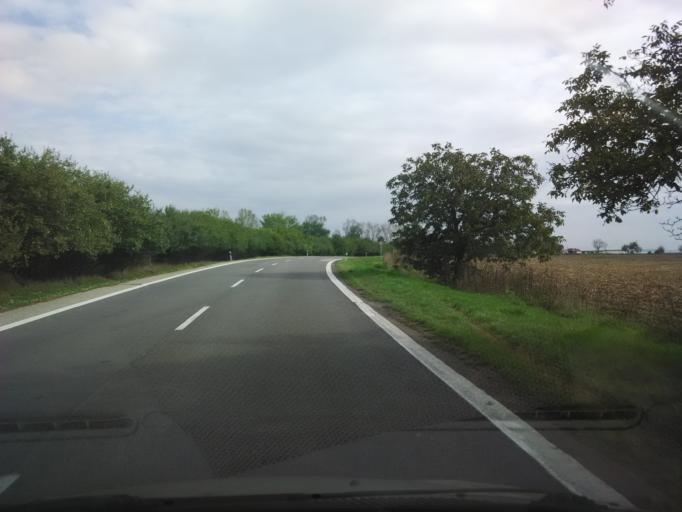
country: SK
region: Nitriansky
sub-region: Okres Nitra
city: Vrable
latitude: 48.2909
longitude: 18.2073
